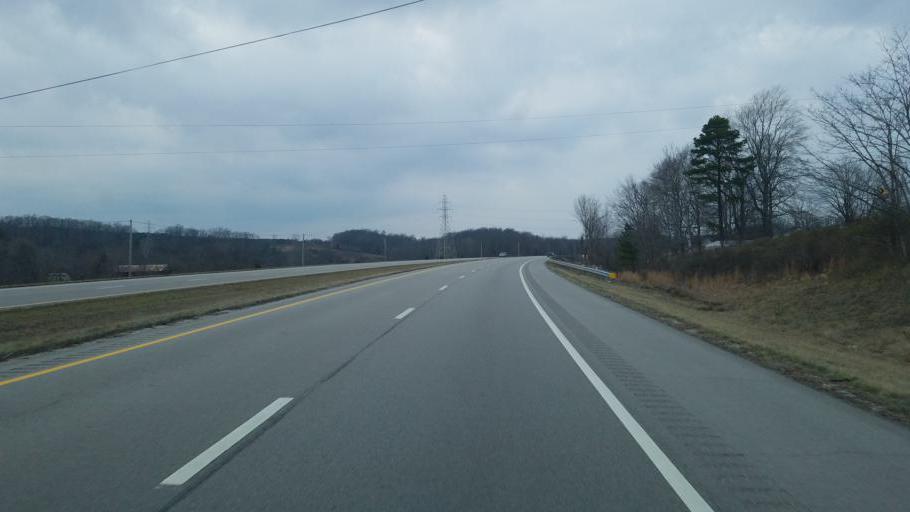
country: US
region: Ohio
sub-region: Jackson County
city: Oak Hill
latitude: 38.8855
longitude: -82.4242
